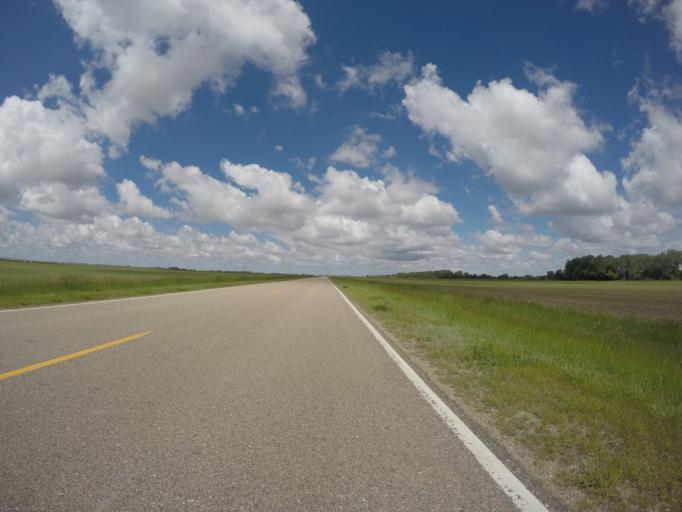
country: US
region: Nebraska
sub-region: Buffalo County
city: Kearney
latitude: 40.6570
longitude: -99.2383
